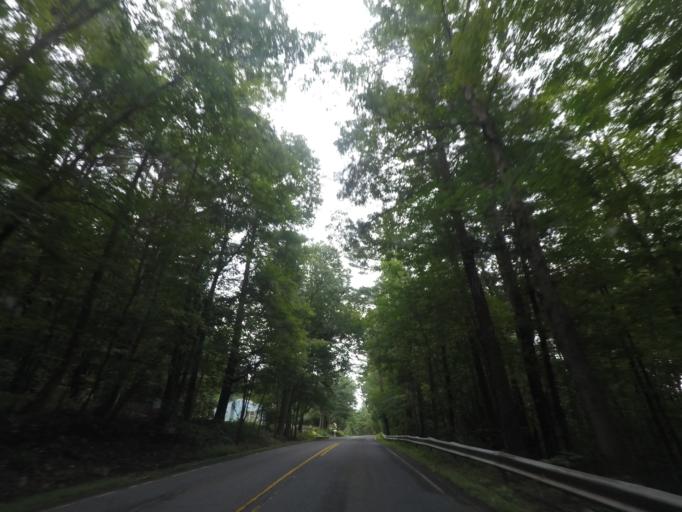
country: US
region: New York
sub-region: Columbia County
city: Chatham
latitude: 42.4187
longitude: -73.5417
